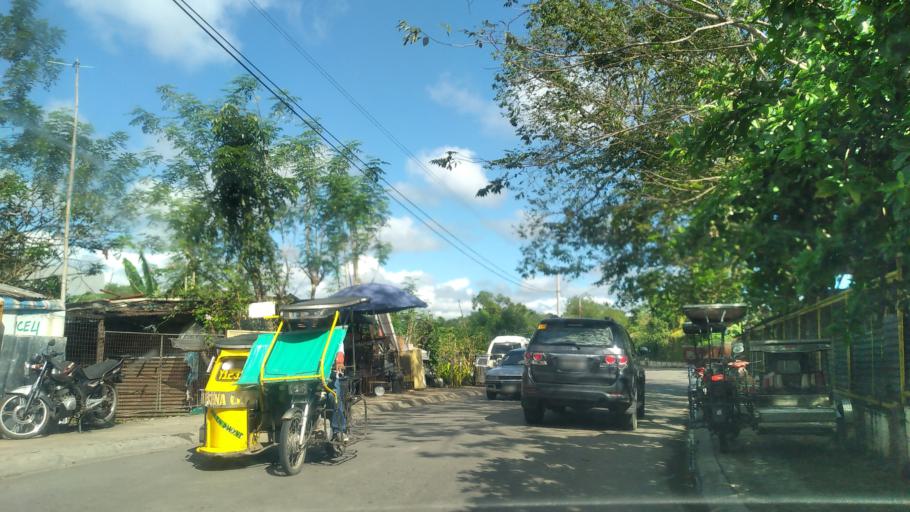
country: PH
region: Calabarzon
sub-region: Province of Quezon
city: Lucena
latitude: 13.9416
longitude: 121.6114
